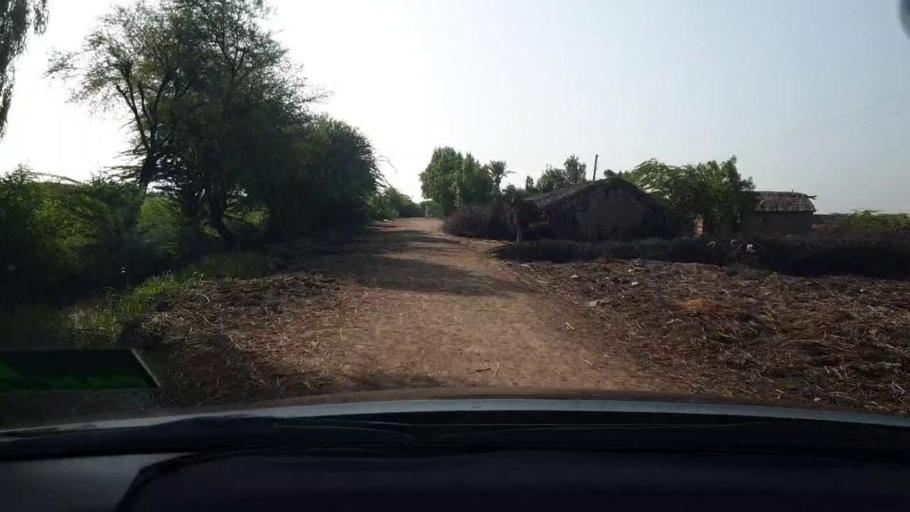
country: PK
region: Sindh
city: Tando Bago
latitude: 24.8003
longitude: 69.0185
